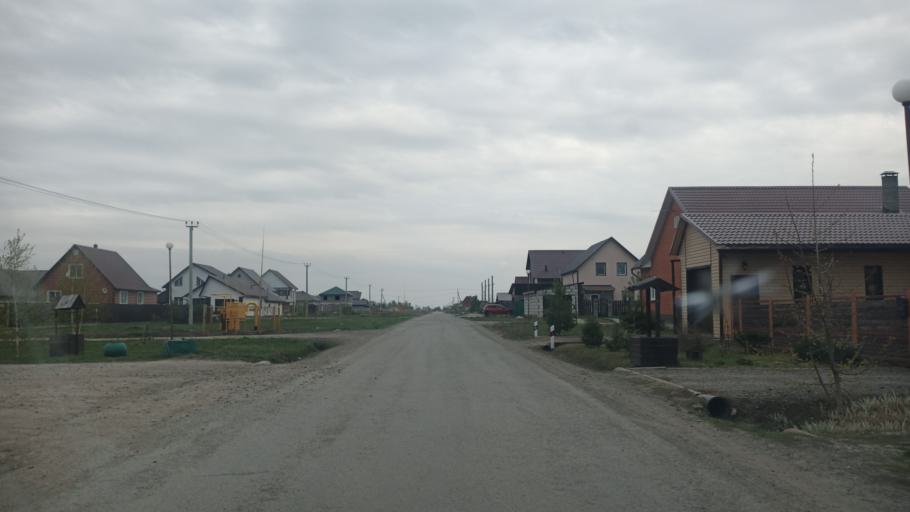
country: RU
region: Altai Krai
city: Yuzhnyy
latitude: 53.2227
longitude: 83.6909
